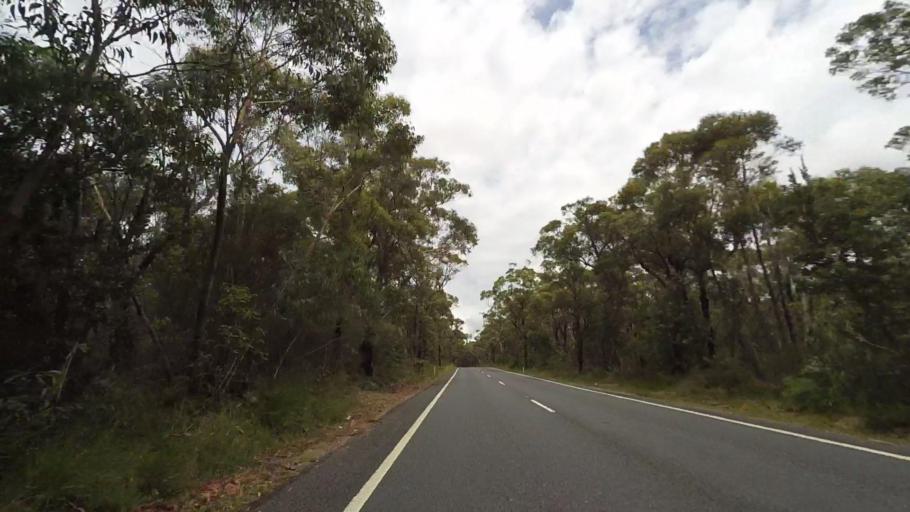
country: AU
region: New South Wales
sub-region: Sutherland Shire
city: Grays Point
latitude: -34.0955
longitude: 151.0612
